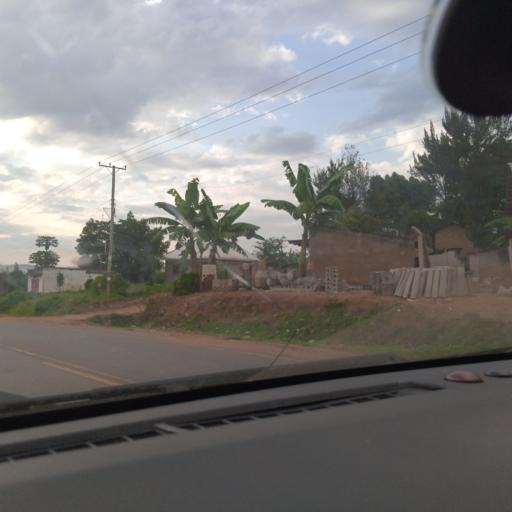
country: UG
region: Central Region
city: Masaka
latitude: -0.3367
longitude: 31.6919
